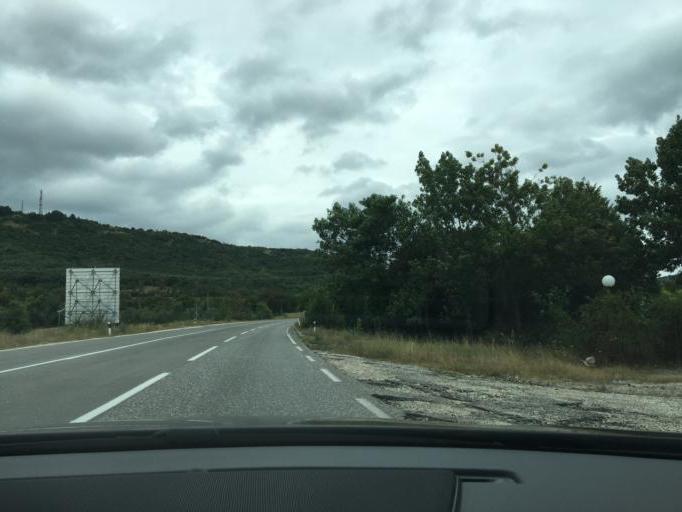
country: MK
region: Opstina Rankovce
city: Rankovce
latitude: 42.1541
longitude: 22.0500
